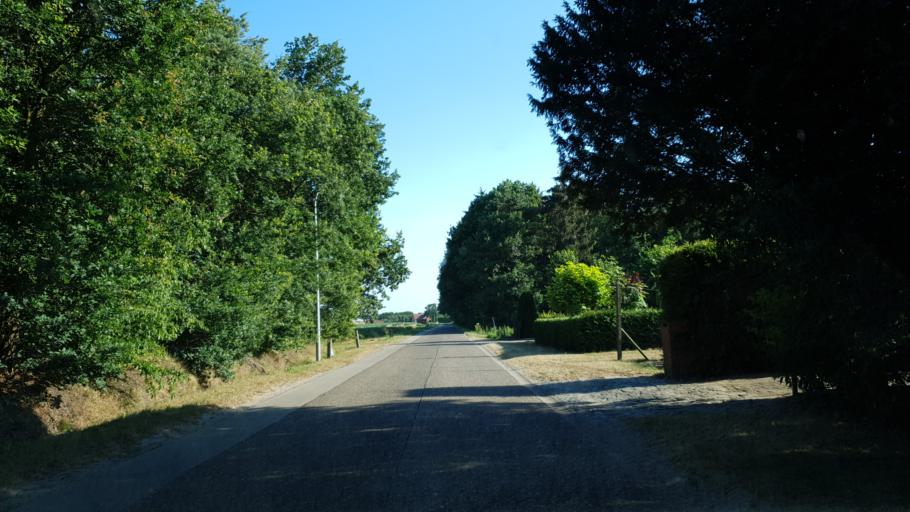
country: BE
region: Flanders
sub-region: Provincie Antwerpen
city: Merksplas
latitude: 51.3866
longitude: 4.8582
